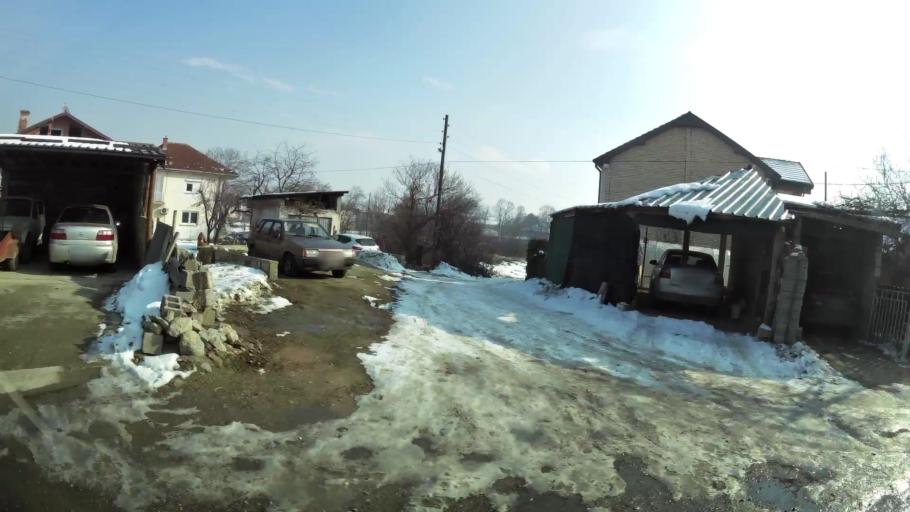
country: MK
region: Suto Orizari
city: Suto Orizare
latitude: 42.0267
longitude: 21.3809
